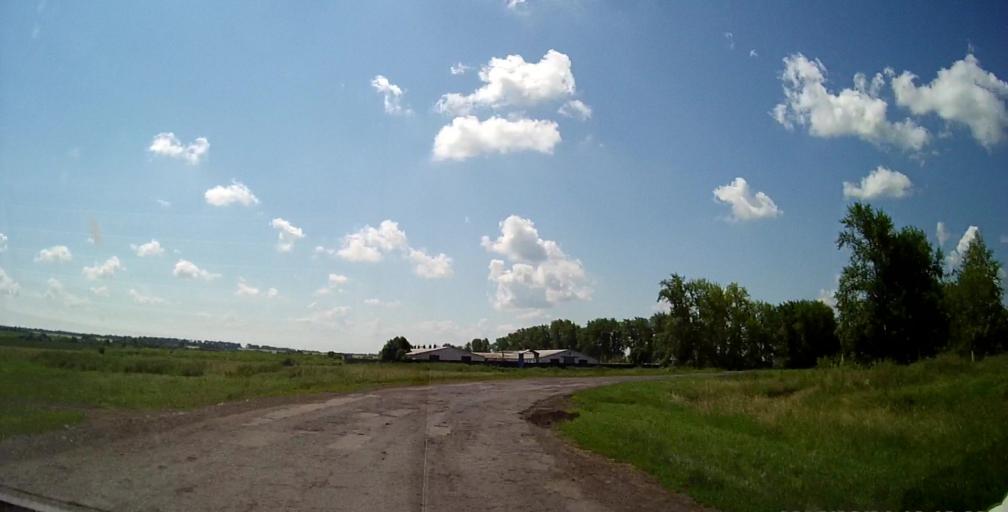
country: RU
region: Lipetsk
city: Chaplygin
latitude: 53.3165
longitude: 39.9600
